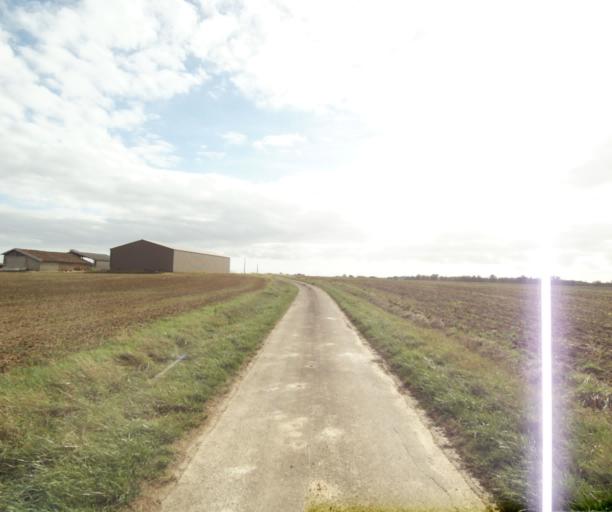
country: FR
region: Midi-Pyrenees
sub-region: Departement du Tarn-et-Garonne
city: Finhan
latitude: 43.9066
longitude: 1.1043
